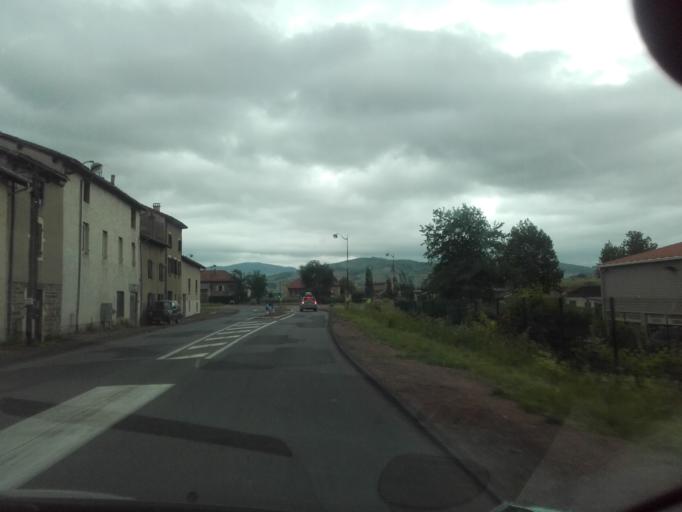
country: FR
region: Rhone-Alpes
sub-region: Departement du Rhone
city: Charentay
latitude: 46.1198
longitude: 4.6780
